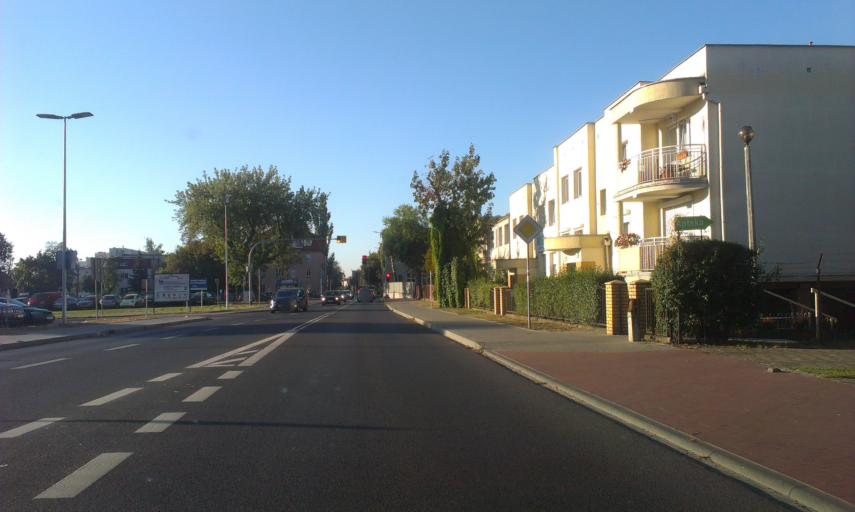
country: PL
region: Kujawsko-Pomorskie
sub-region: Torun
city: Torun
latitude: 53.0258
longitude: 18.6015
